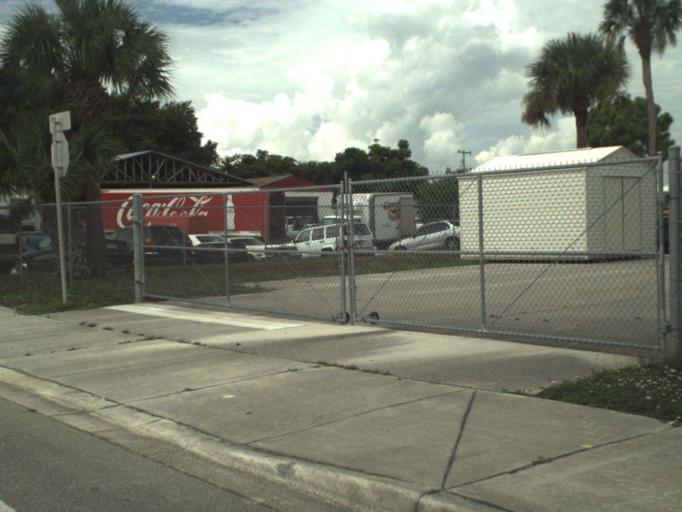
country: US
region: Florida
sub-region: Saint Lucie County
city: Fort Pierce North
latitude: 27.4870
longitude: -80.3503
